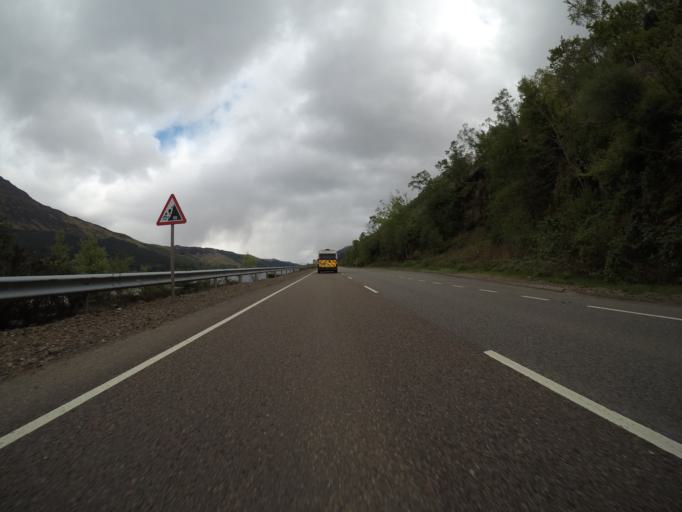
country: GB
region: Scotland
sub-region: Highland
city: Spean Bridge
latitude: 56.9988
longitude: -4.8542
